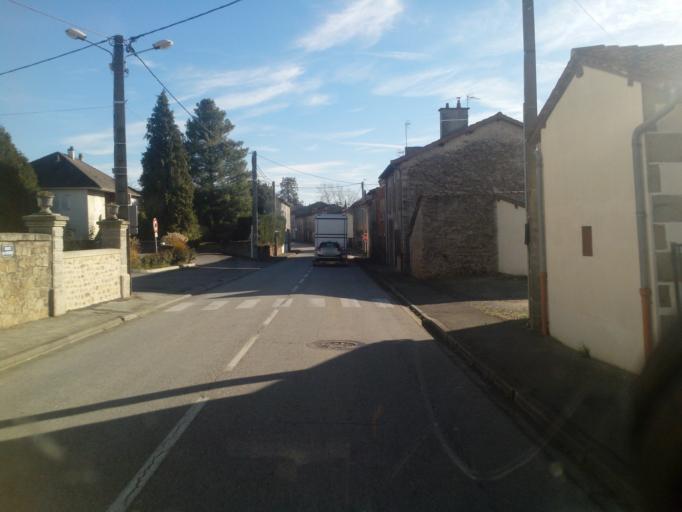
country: FR
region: Limousin
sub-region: Departement de la Haute-Vienne
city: Bellac
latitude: 46.0696
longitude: 1.1047
